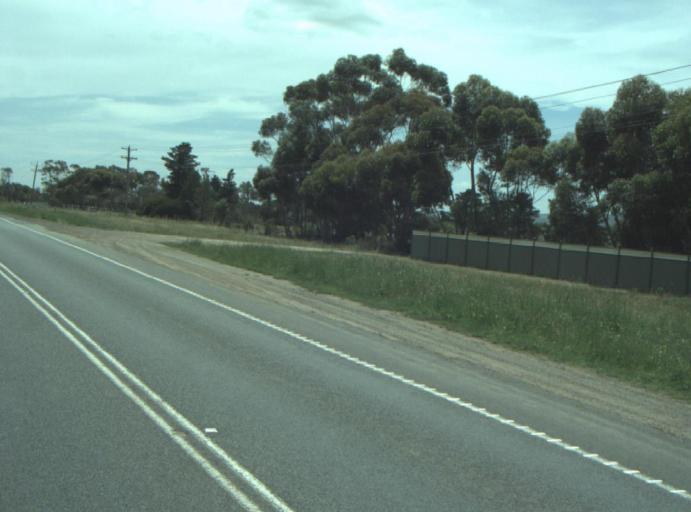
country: AU
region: Victoria
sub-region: Greater Geelong
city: Lara
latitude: -38.0294
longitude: 144.3546
